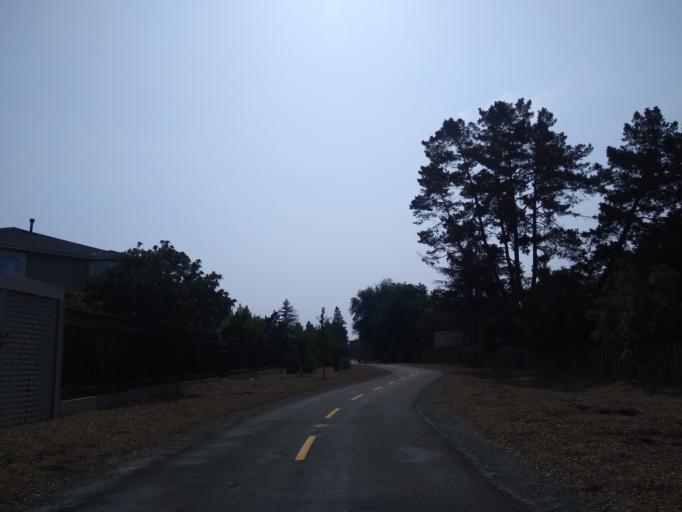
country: US
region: California
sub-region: Santa Clara County
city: Buena Vista
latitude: 37.3100
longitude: -121.8935
